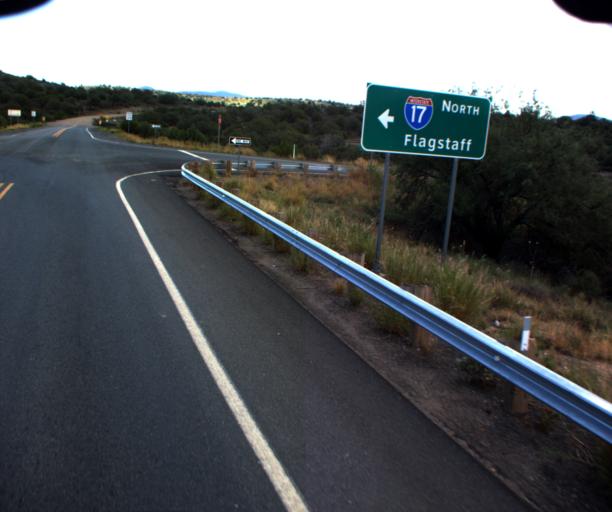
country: US
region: Arizona
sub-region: Yavapai County
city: Camp Verde
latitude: 34.5142
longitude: -111.9918
